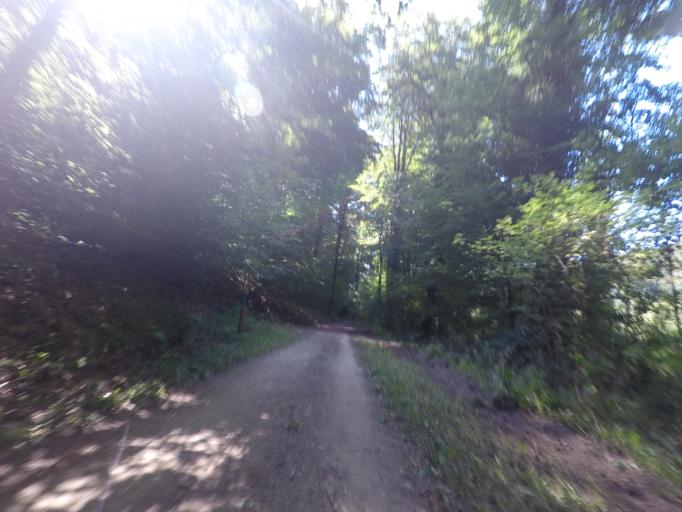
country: LU
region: Luxembourg
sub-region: Canton de Capellen
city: Kopstal
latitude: 49.6484
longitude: 6.0584
